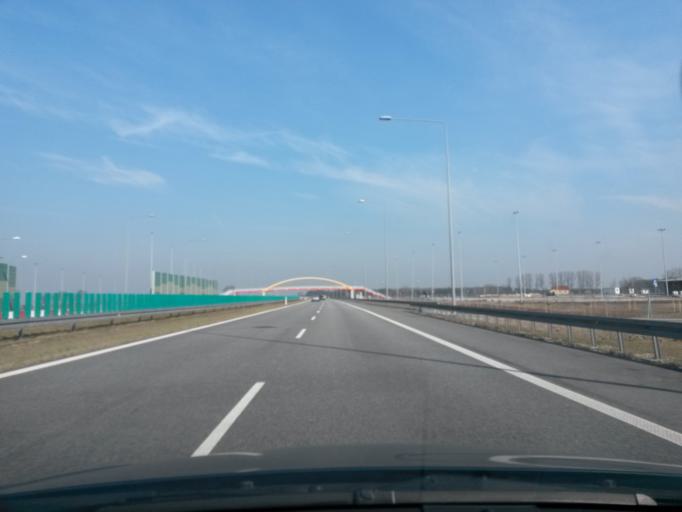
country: PL
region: Lodz Voivodeship
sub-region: Powiat kutnowski
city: Krzyzanow
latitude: 52.1829
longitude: 19.4873
